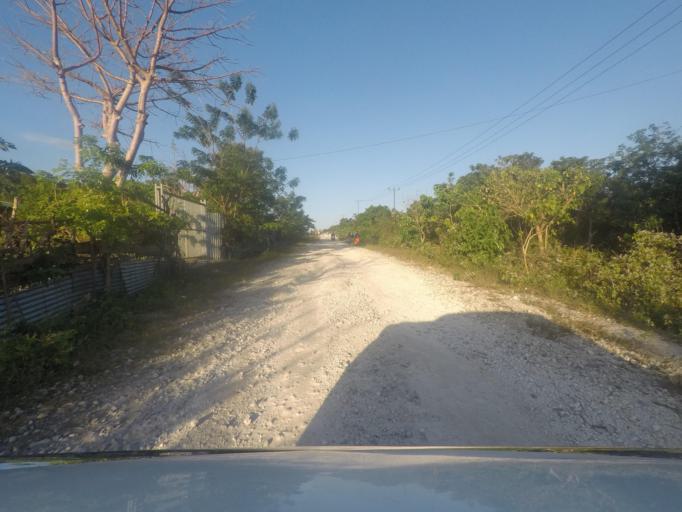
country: TL
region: Lautem
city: Lospalos
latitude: -8.3991
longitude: 127.2017
